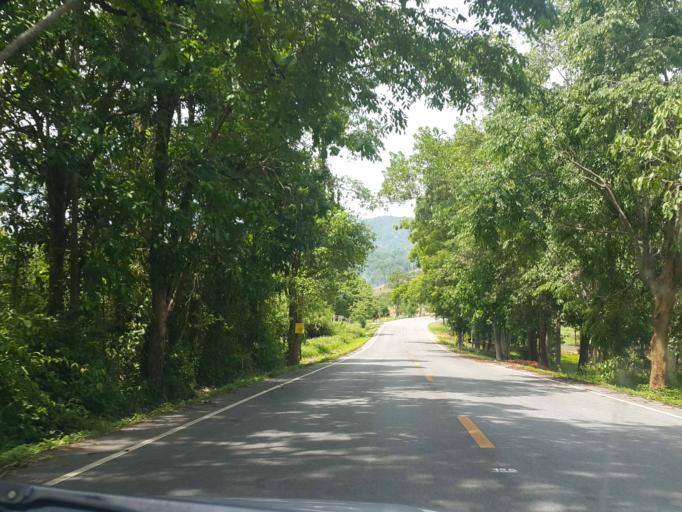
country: TH
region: Nan
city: Ban Luang
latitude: 18.8659
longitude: 100.4667
